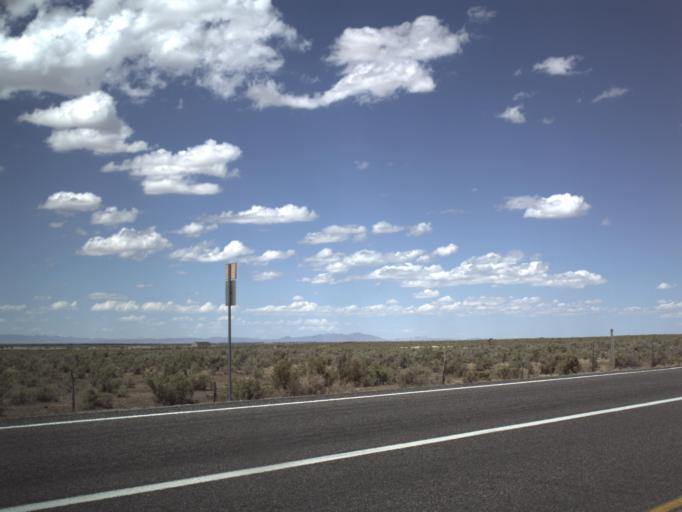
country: US
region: Utah
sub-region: Millard County
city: Fillmore
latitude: 39.1565
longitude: -112.4090
